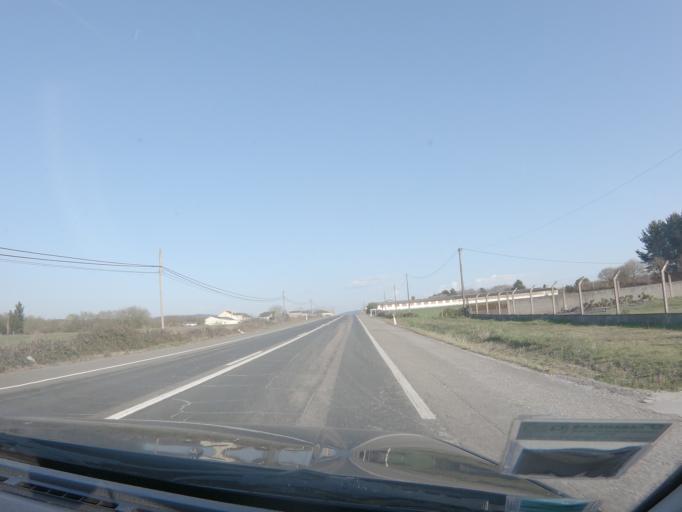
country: ES
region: Galicia
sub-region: Provincia de Lugo
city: Corgo
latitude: 42.9351
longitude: -7.4057
